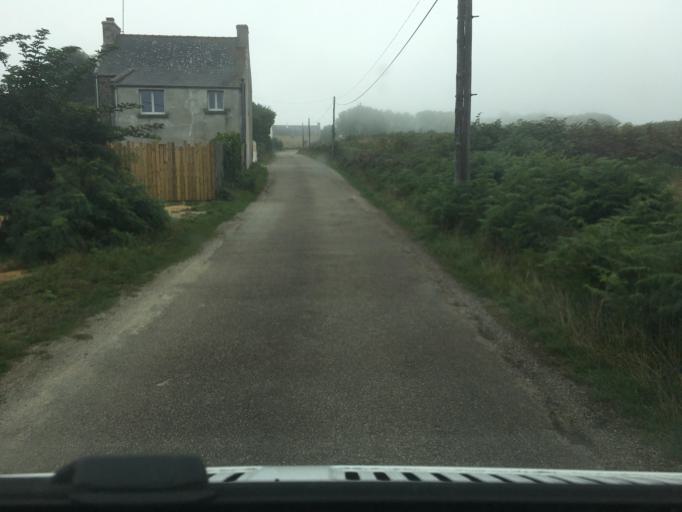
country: FR
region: Brittany
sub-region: Departement du Finistere
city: Plogoff
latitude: 48.0380
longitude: -4.6915
